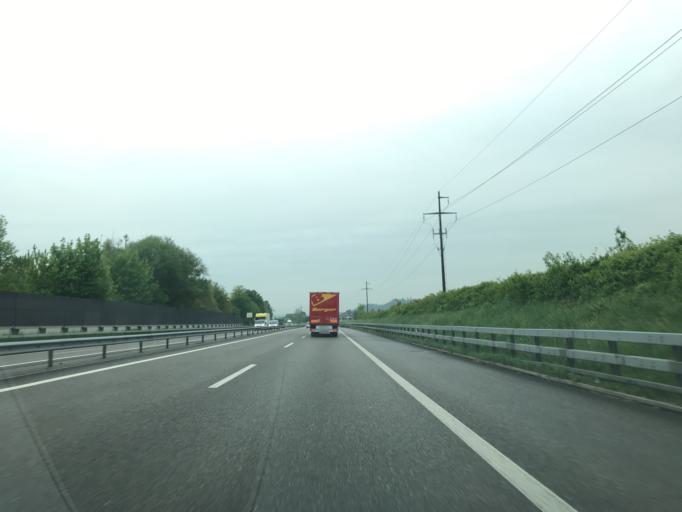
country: CH
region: Aargau
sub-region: Bezirk Zofingen
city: Strengelbach
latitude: 47.2780
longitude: 7.9379
